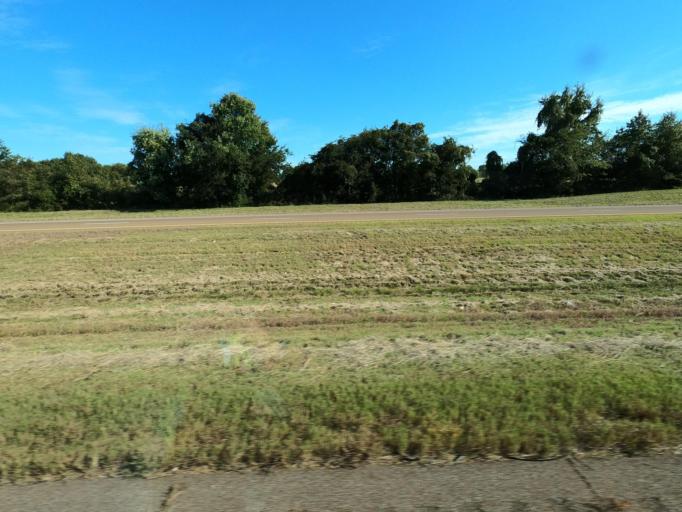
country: US
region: Tennessee
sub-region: Dyer County
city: Newbern
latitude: 36.1475
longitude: -89.2568
